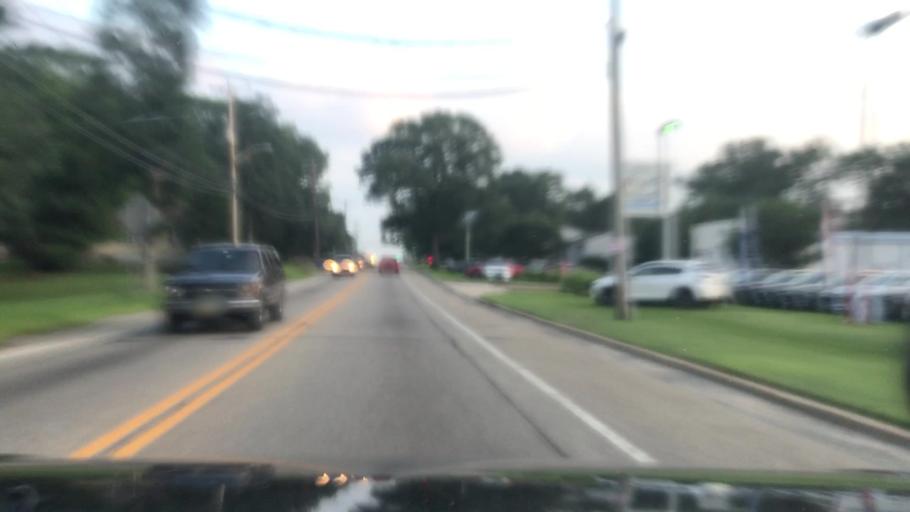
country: US
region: New Jersey
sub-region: Ocean County
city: Silver Ridge
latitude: 39.9965
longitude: -74.2119
